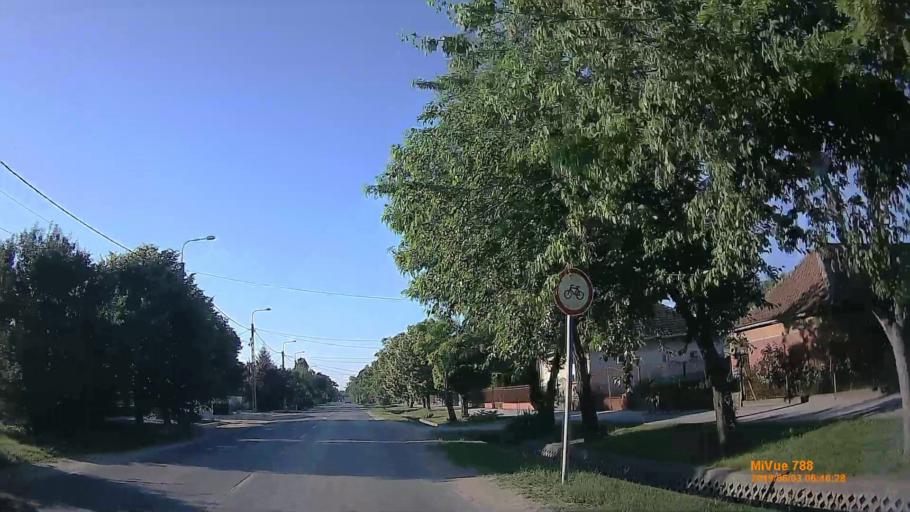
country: HU
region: Pest
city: Bugyi
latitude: 47.2311
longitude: 19.1437
